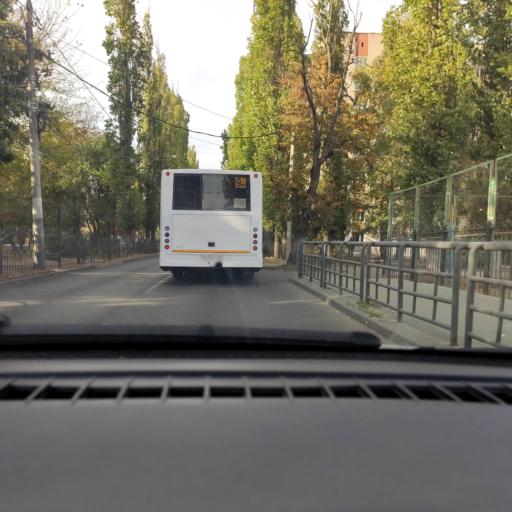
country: RU
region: Voronezj
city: Voronezh
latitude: 51.7141
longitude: 39.2280
